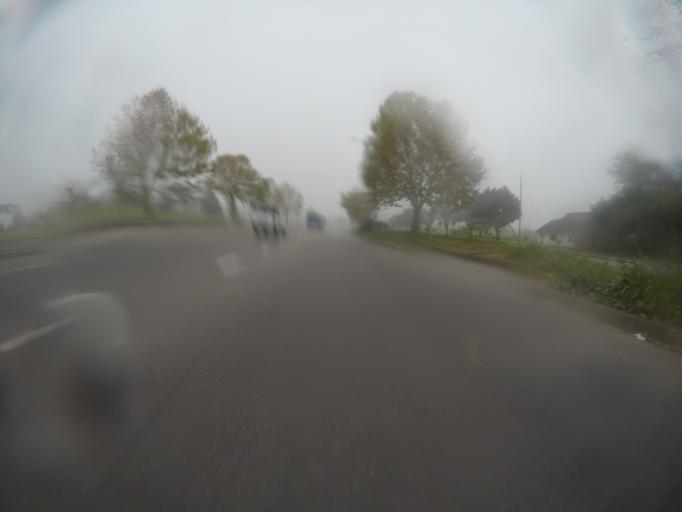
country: ZA
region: Western Cape
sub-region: Eden District Municipality
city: George
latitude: -33.9812
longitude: 22.4409
